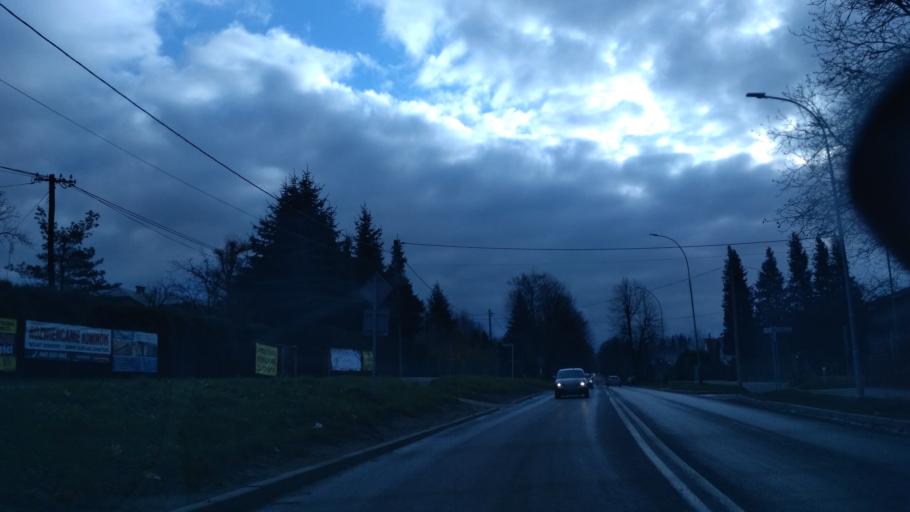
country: PL
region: Subcarpathian Voivodeship
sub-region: Powiat lancucki
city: Lancut
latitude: 50.0764
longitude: 22.2363
